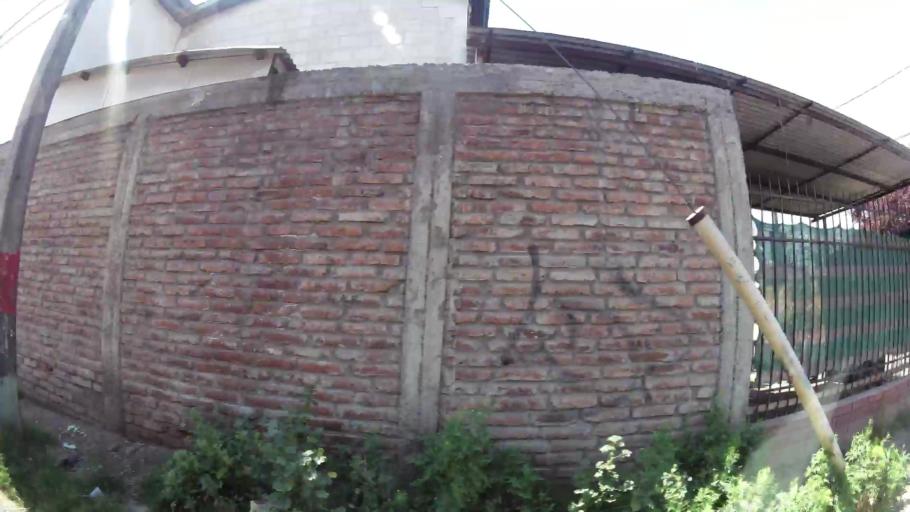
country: CL
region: Santiago Metropolitan
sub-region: Provincia de Santiago
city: La Pintana
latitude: -33.5610
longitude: -70.6353
